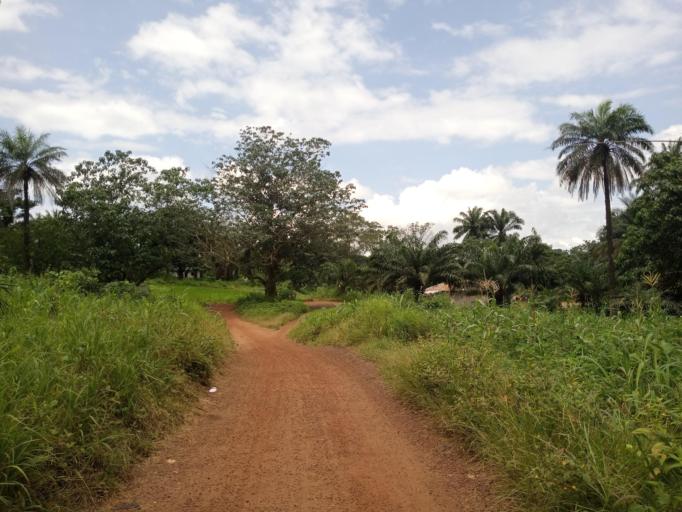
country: SL
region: Northern Province
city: Kamakwie
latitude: 9.4888
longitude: -12.2450
